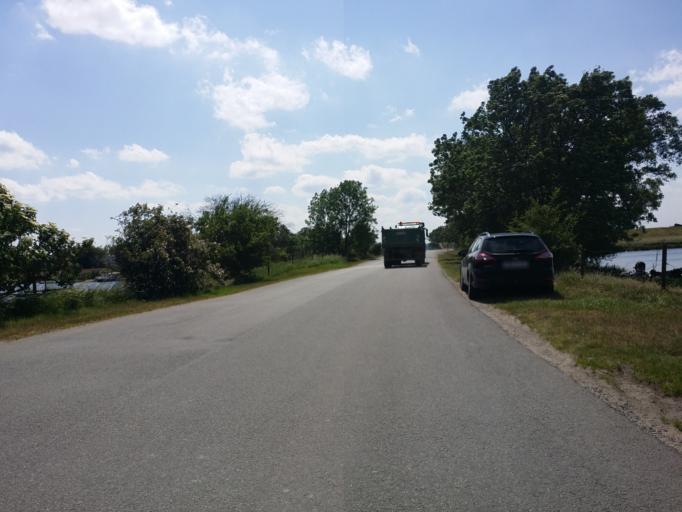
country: DE
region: Lower Saxony
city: Lemwerder
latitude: 53.1209
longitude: 8.6459
